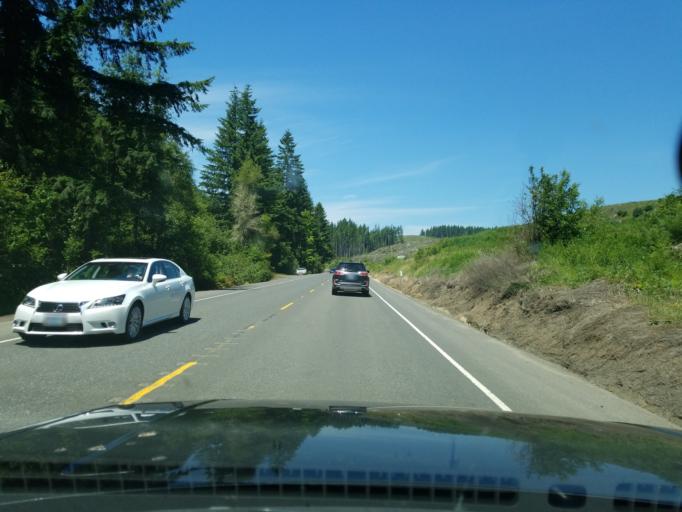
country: US
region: Oregon
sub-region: Columbia County
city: Vernonia
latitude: 45.7679
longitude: -123.3184
